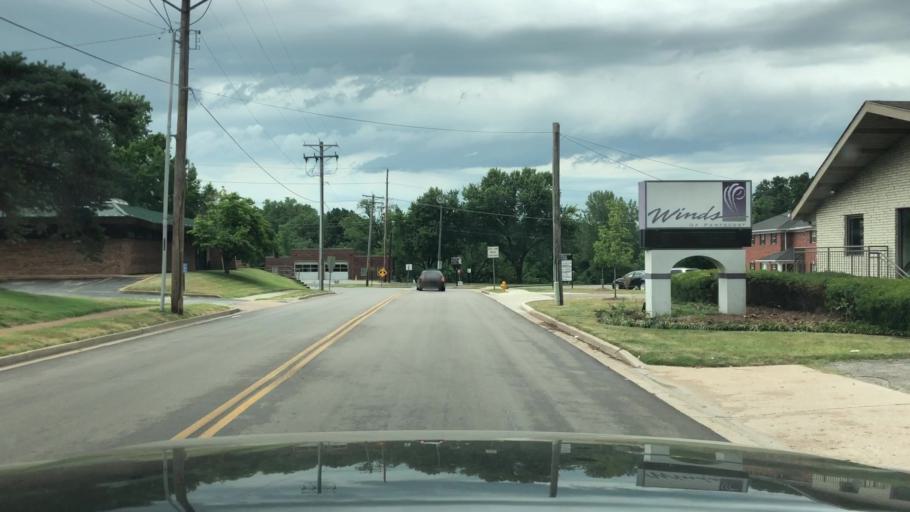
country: US
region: Missouri
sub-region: Saint Charles County
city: Saint Charles
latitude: 38.7738
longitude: -90.4991
